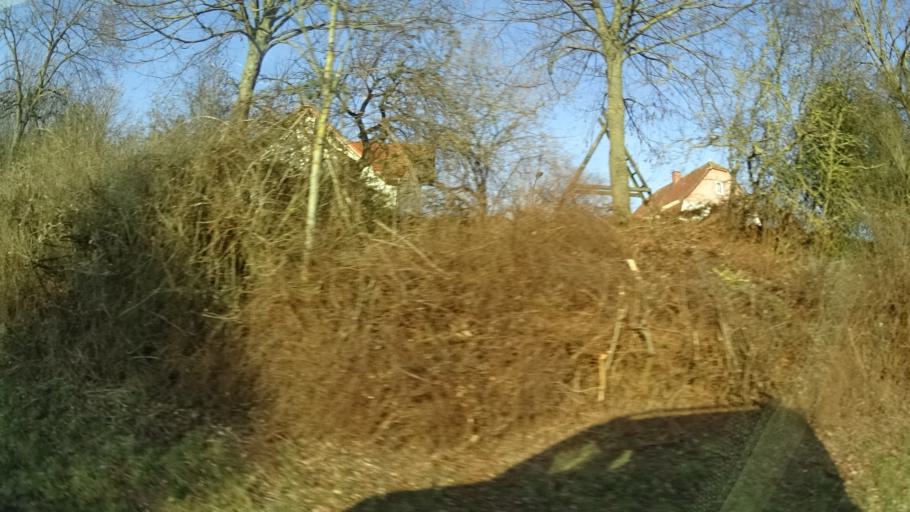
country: DE
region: Hesse
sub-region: Regierungsbezirk Darmstadt
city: Schluchtern
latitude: 50.3215
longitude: 9.5963
